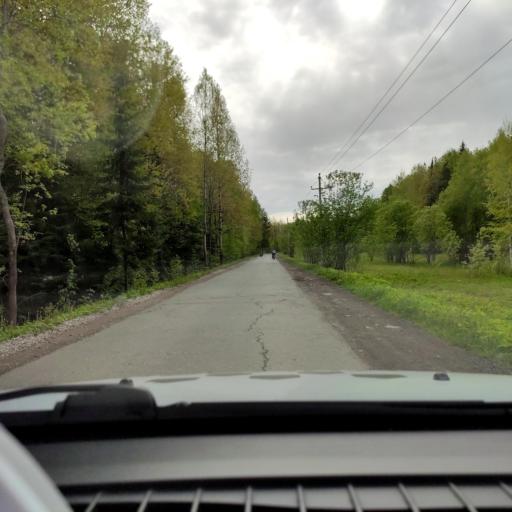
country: RU
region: Perm
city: Novyye Lyady
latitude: 58.0413
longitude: 56.6291
